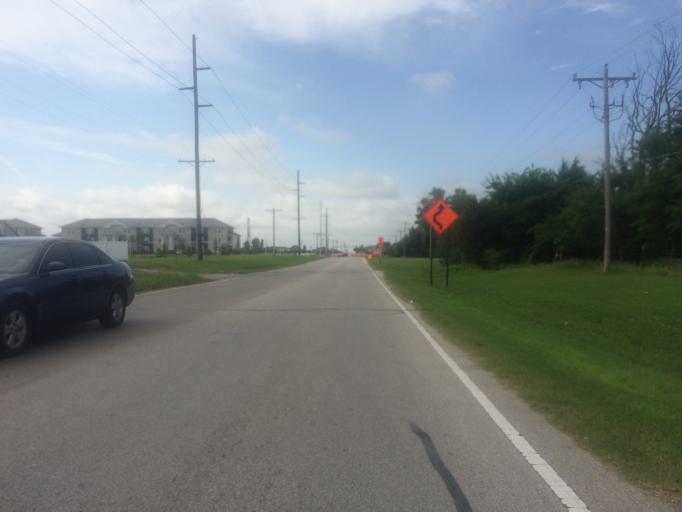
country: US
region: Oklahoma
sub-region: Cleveland County
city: Norman
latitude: 35.1792
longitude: -97.4237
